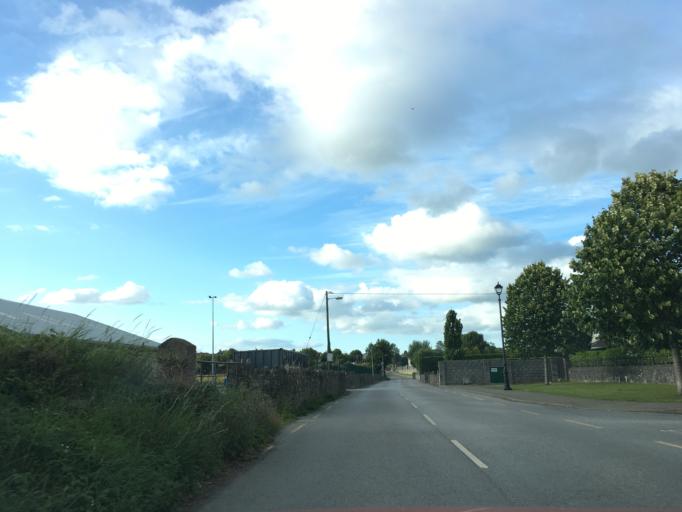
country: IE
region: Munster
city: Cashel
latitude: 52.5064
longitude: -7.8863
